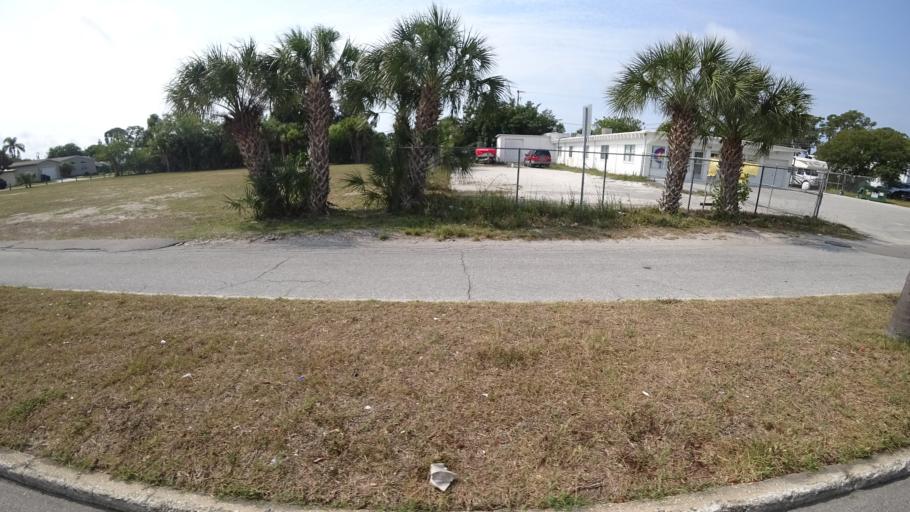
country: US
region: Florida
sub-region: Manatee County
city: South Bradenton
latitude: 27.4528
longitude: -82.5744
